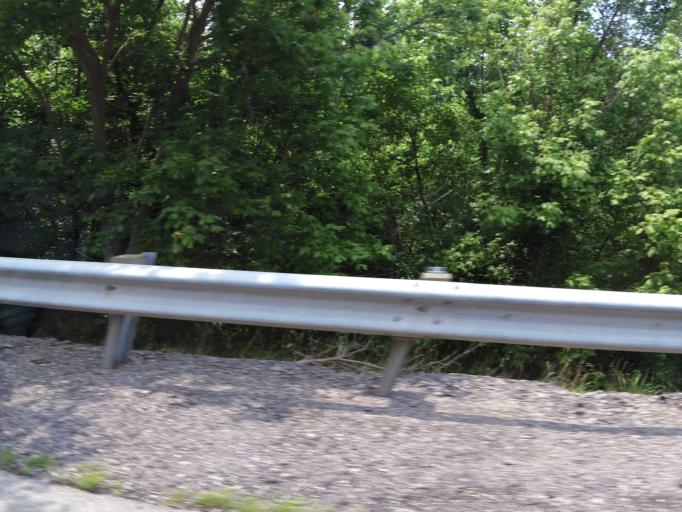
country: US
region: Kentucky
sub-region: Henry County
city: New Castle
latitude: 38.4749
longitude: -85.2726
